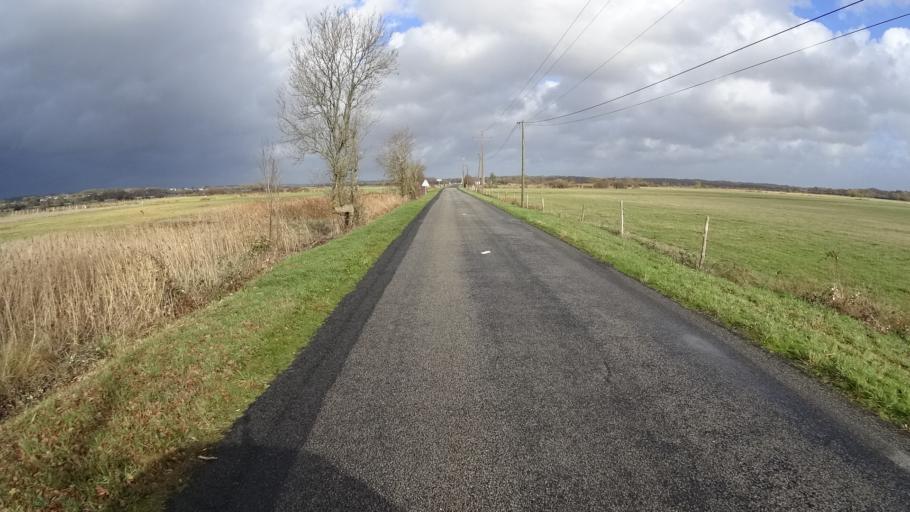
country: FR
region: Brittany
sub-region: Departement du Morbihan
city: Rieux
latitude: 47.5731
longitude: -2.1053
